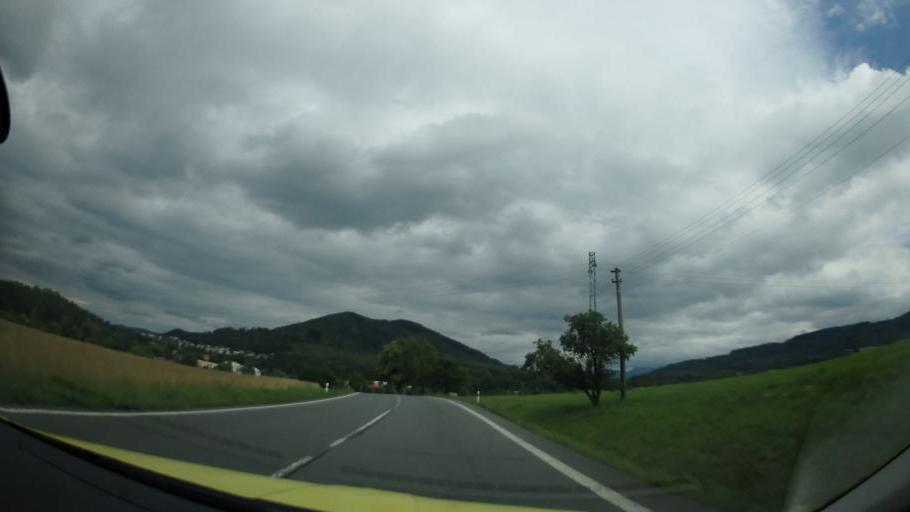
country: CZ
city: Stramberk
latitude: 49.5752
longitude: 18.1186
